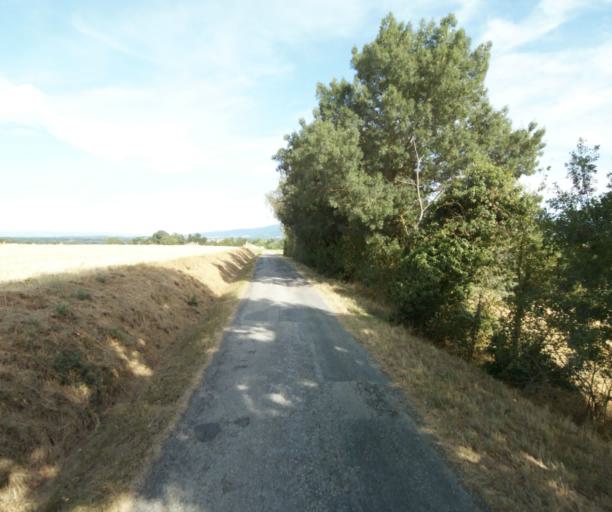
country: FR
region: Midi-Pyrenees
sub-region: Departement du Tarn
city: Soual
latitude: 43.5315
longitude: 2.0700
